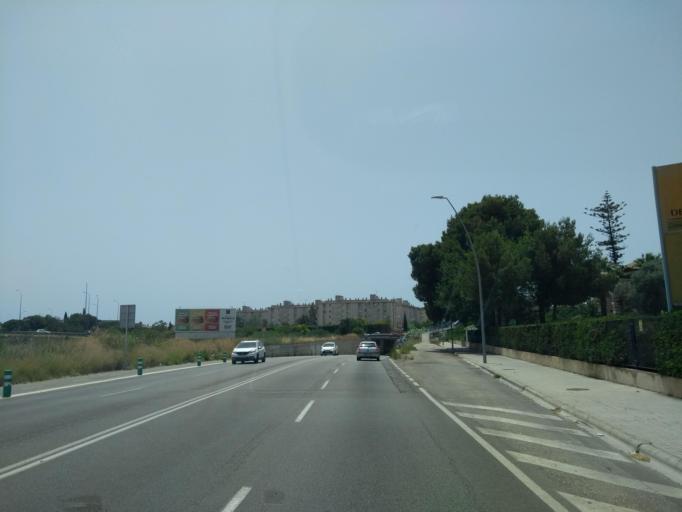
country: ES
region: Balearic Islands
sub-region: Illes Balears
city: Palma
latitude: 39.5897
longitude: 2.6663
